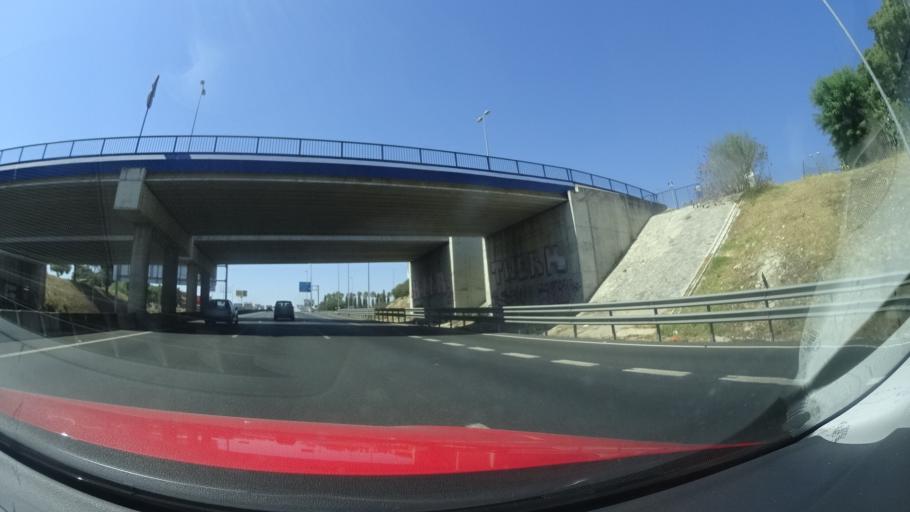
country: ES
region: Andalusia
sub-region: Provincia de Sevilla
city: Castilleja de la Cuesta
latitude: 37.3819
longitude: -6.0448
